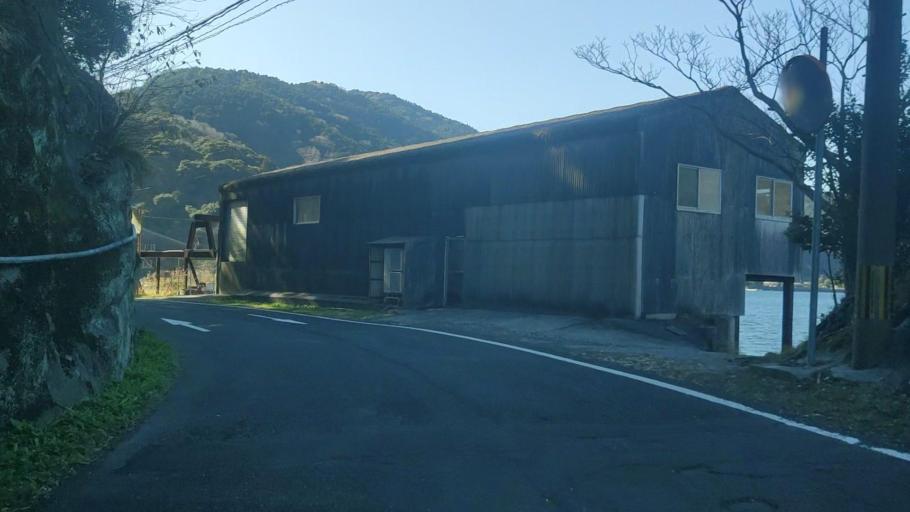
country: JP
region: Oita
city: Saiki
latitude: 32.8364
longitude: 131.9535
